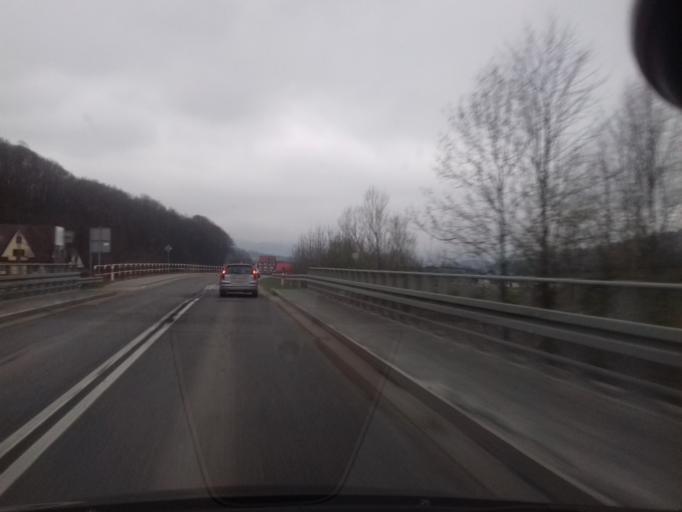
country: PL
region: Lesser Poland Voivodeship
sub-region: Powiat limanowski
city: Mszana Dolna
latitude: 49.7036
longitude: 20.0327
